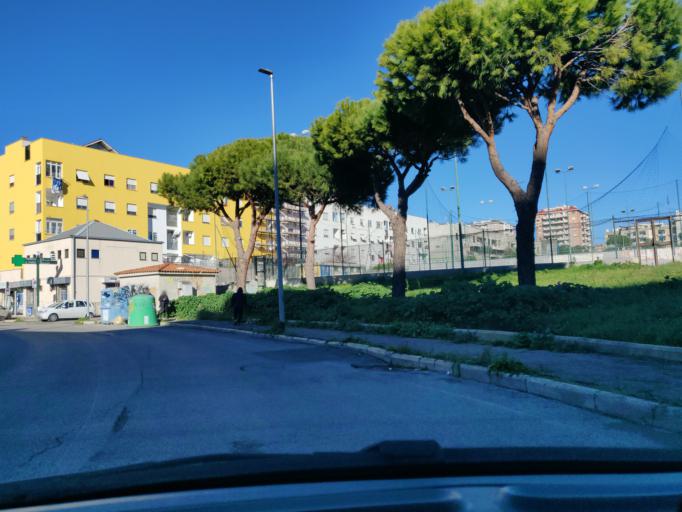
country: IT
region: Latium
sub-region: Citta metropolitana di Roma Capitale
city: Civitavecchia
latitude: 42.0970
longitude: 11.8226
